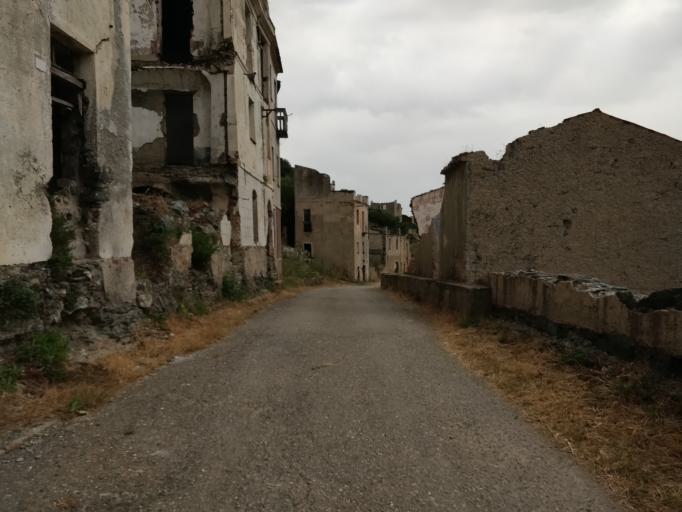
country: IT
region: Sardinia
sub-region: Provincia di Ogliastra
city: Gairo Sant'Elena
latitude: 39.8476
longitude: 9.4998
